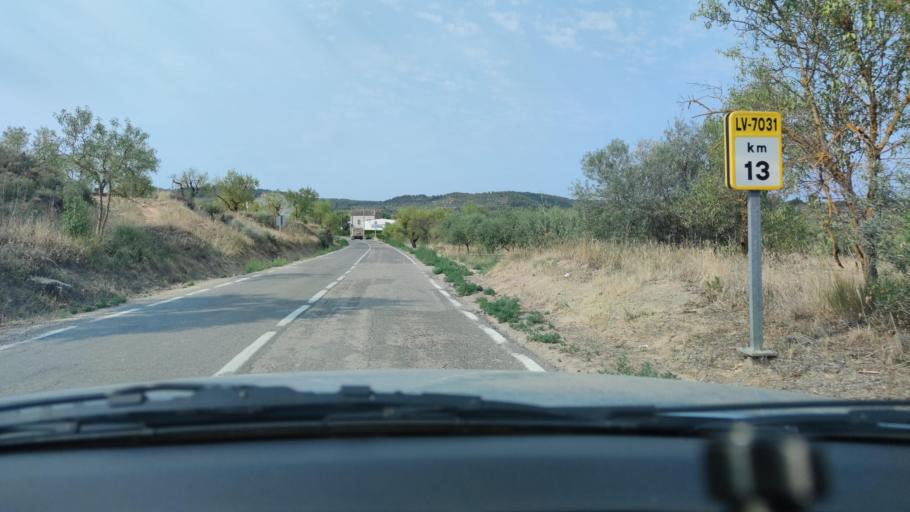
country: ES
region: Catalonia
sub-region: Provincia de Lleida
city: Juncosa
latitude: 41.4295
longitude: 0.8609
